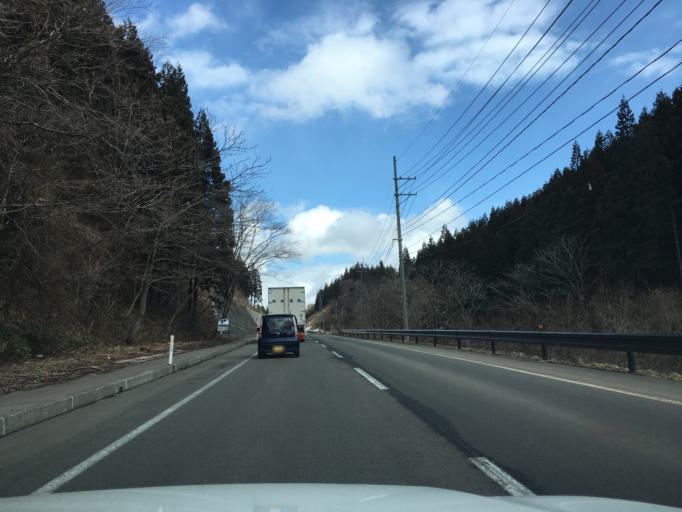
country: JP
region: Akita
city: Takanosu
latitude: 40.1010
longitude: 140.3456
